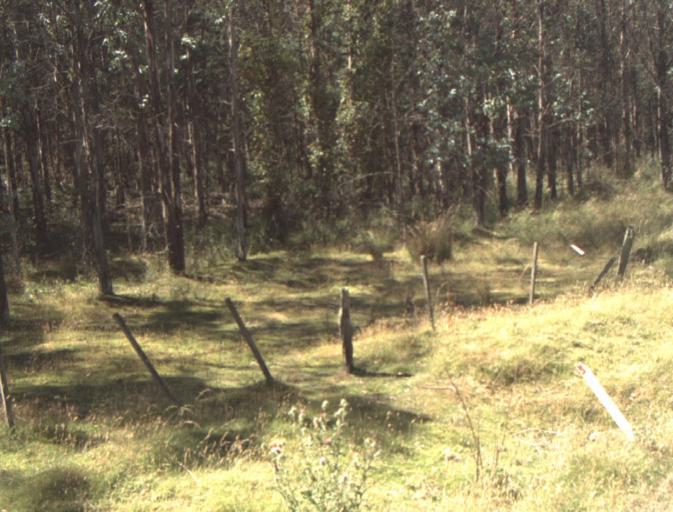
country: AU
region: Tasmania
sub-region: Dorset
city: Scottsdale
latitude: -41.2686
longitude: 147.3520
